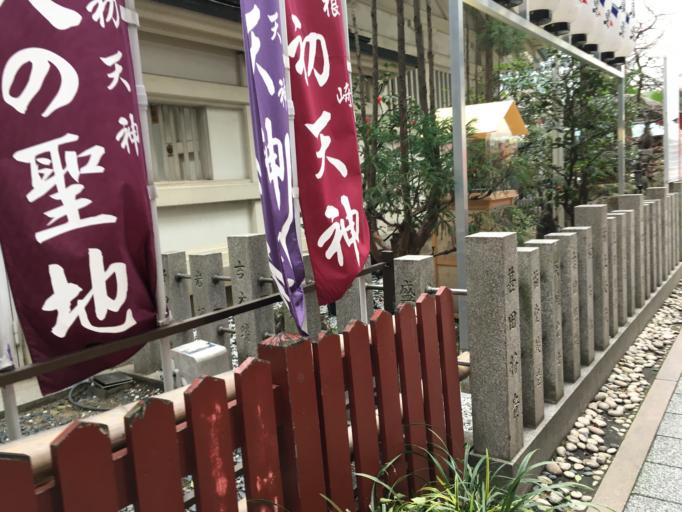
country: JP
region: Osaka
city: Osaka-shi
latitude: 34.6994
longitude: 135.5006
